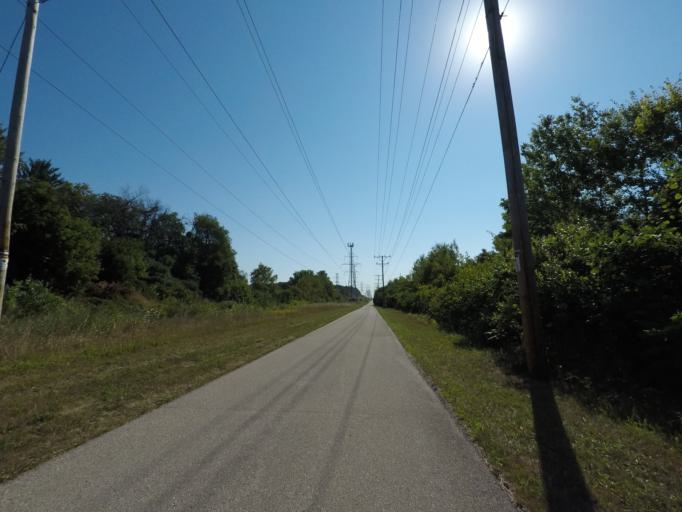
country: US
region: Wisconsin
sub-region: Waukesha County
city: Waukesha
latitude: 43.0099
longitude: -88.1816
